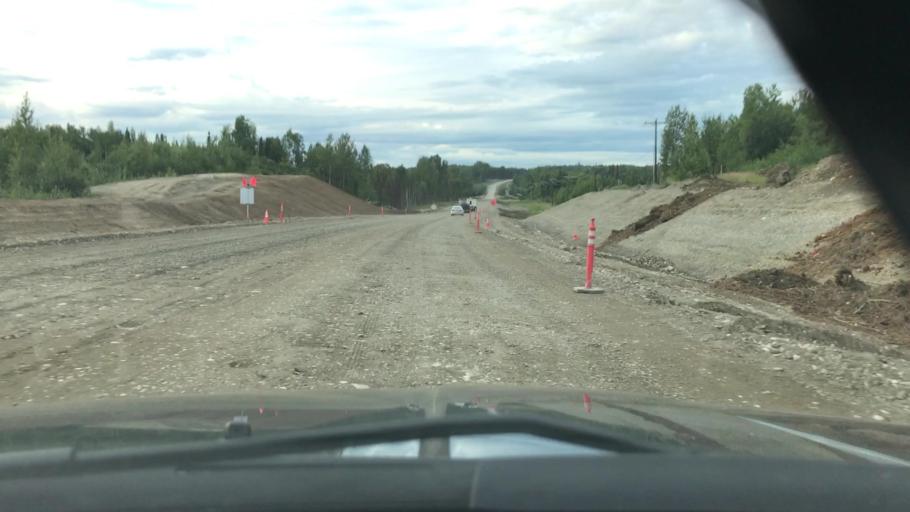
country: US
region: Alaska
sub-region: Matanuska-Susitna Borough
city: Y
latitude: 62.0952
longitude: -150.0618
